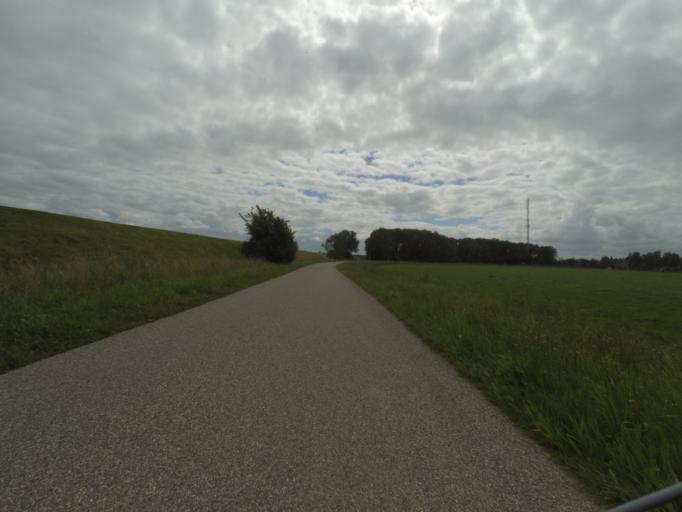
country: NL
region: Friesland
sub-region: Gemeente Kollumerland en Nieuwkruisland
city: Kollum
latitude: 53.3273
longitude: 6.1549
